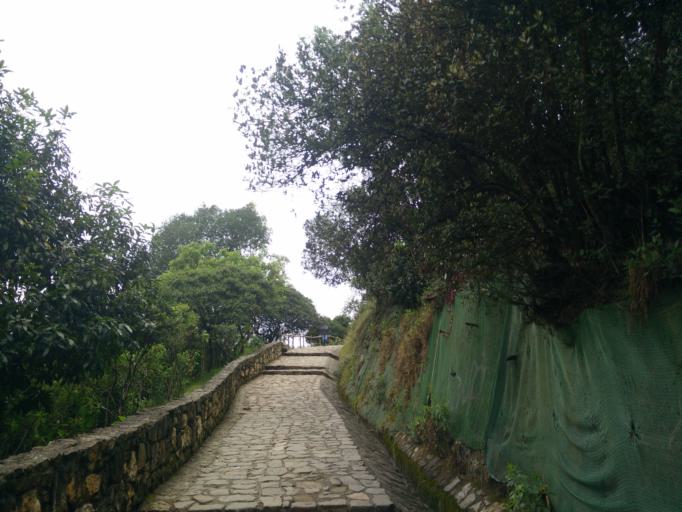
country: CO
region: Bogota D.C.
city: Bogota
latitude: 4.6078
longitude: -74.0597
